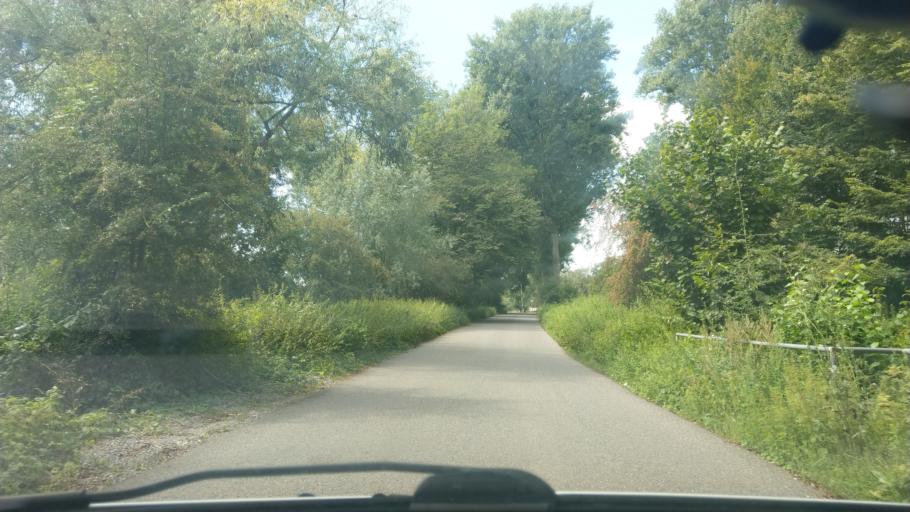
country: DE
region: North Rhine-Westphalia
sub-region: Regierungsbezirk Dusseldorf
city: Dormagen
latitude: 51.1433
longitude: 6.8625
